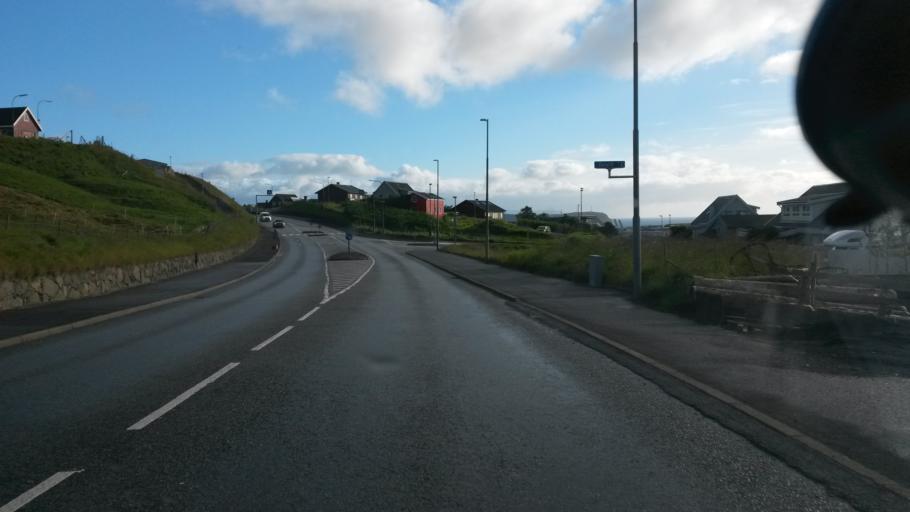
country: FO
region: Streymoy
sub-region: Torshavn
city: Torshavn
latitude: 62.0134
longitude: -6.7892
